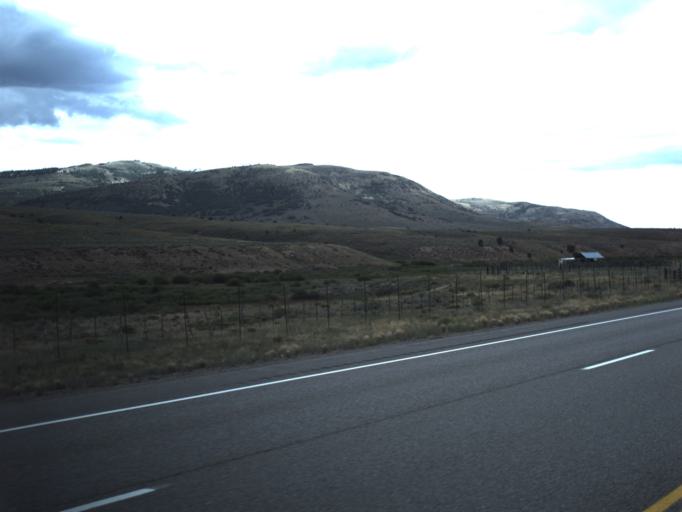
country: US
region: Utah
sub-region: Carbon County
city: Helper
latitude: 39.8995
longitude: -111.0560
